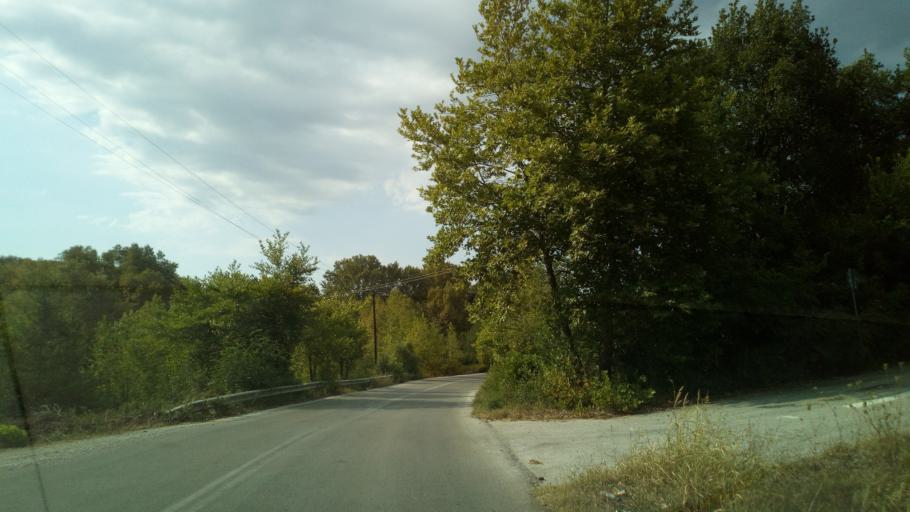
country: GR
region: Central Macedonia
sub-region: Nomos Thessalonikis
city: Gerakarou
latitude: 40.5862
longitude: 23.2539
